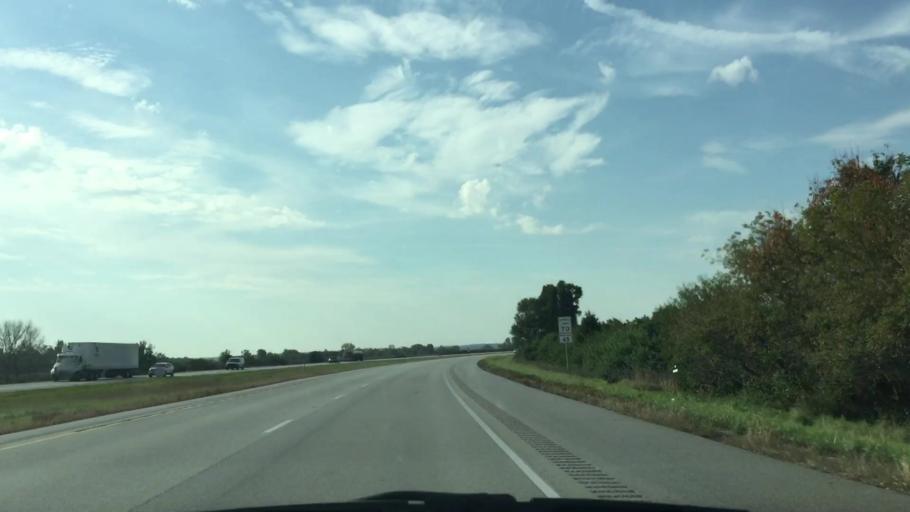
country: US
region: Illinois
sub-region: Whiteside County
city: Erie
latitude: 41.5992
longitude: -90.1924
